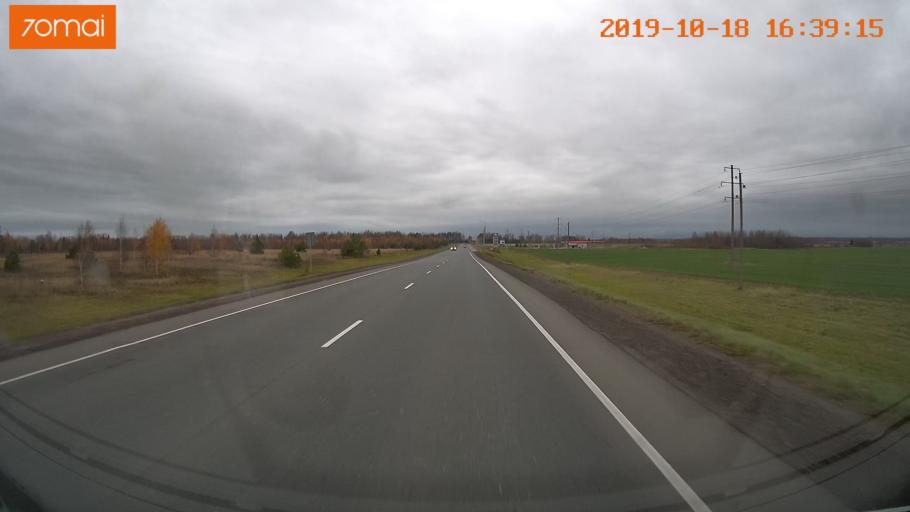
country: RU
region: Vladimir
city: Suzdal'
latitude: 56.4487
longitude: 40.4625
